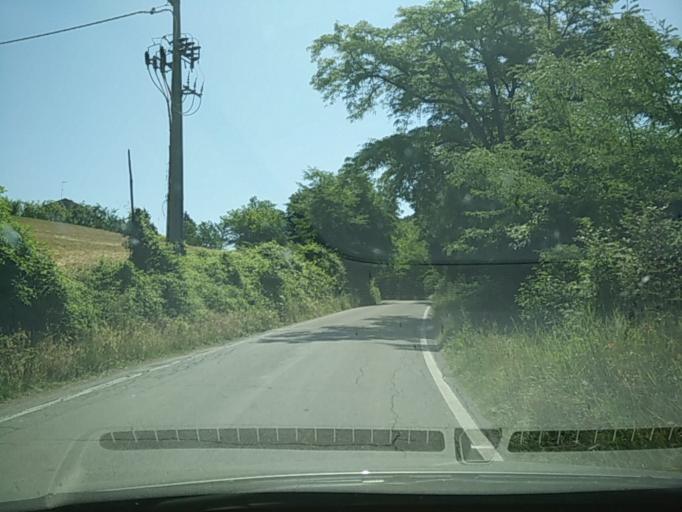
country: IT
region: Lombardy
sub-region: Provincia di Pavia
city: Godiasco
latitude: 44.8949
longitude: 9.0742
